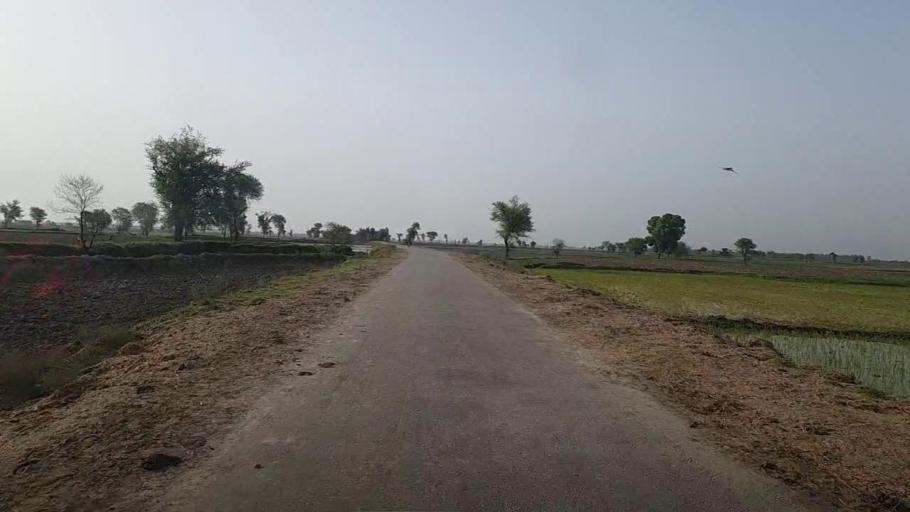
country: PK
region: Sindh
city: Khairpur Nathan Shah
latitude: 27.0988
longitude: 67.7927
